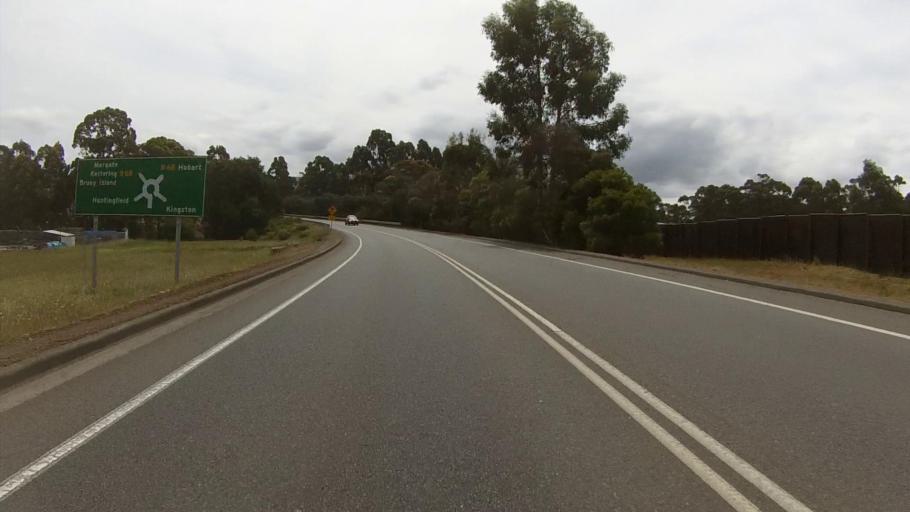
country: AU
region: Tasmania
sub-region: Kingborough
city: Kingston
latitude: -42.9893
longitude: 147.2935
